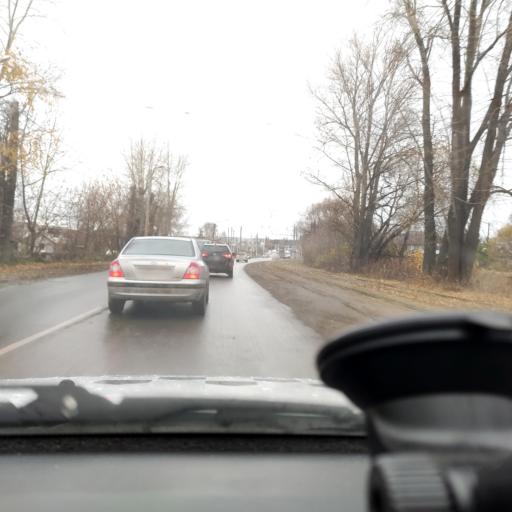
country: RU
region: Perm
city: Kondratovo
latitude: 57.9561
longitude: 56.1348
